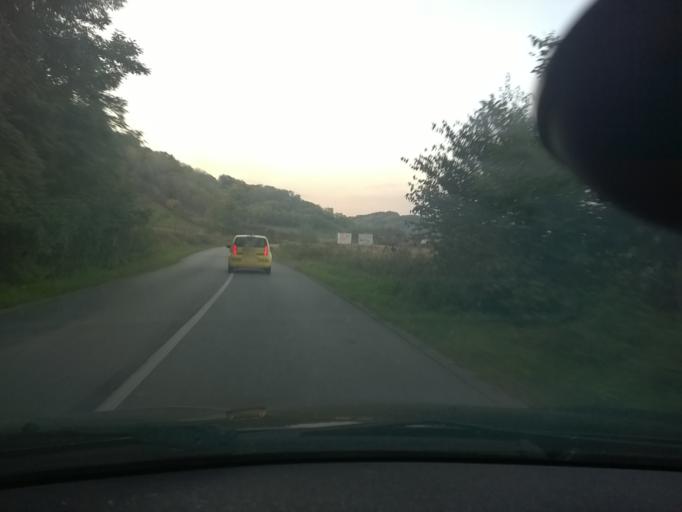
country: HR
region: Krapinsko-Zagorska
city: Zabok
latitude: 46.0474
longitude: 15.9095
